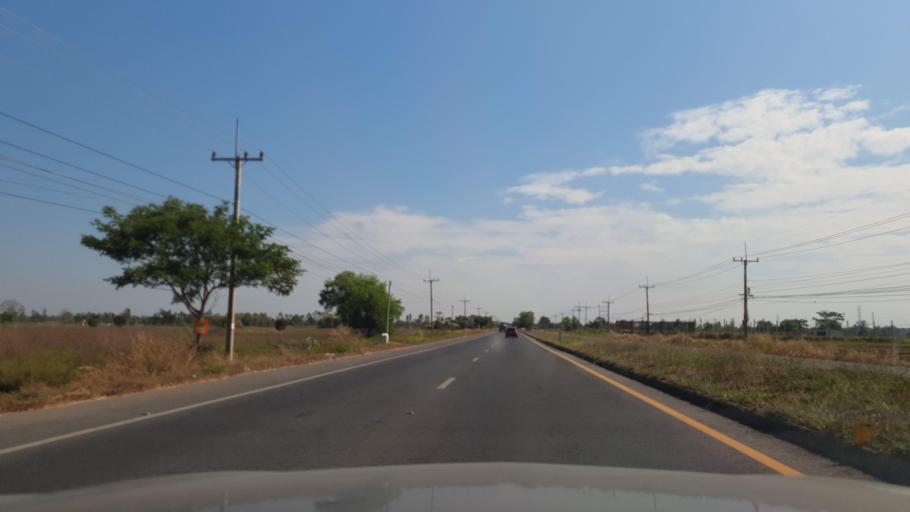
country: TH
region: Maha Sarakham
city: Chiang Yuen
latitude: 16.3750
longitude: 103.1615
